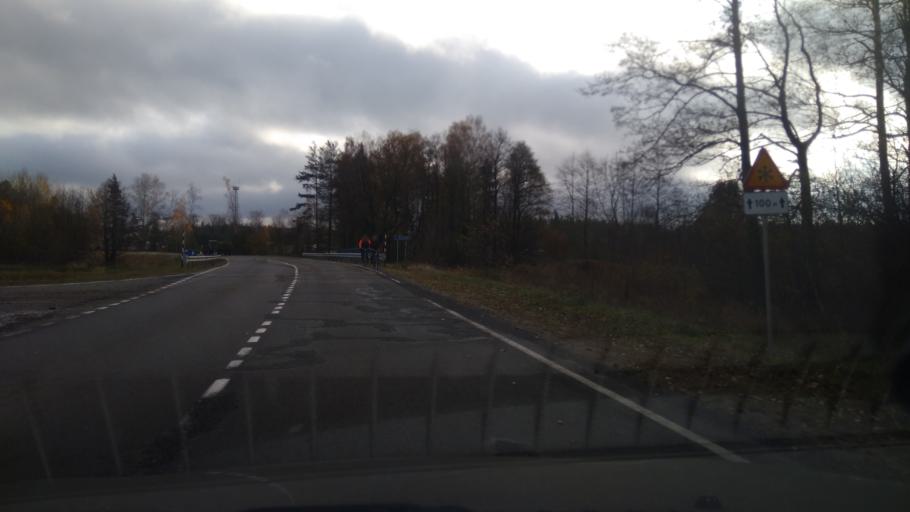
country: BY
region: Minsk
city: Slutsk
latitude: 53.2083
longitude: 27.7645
